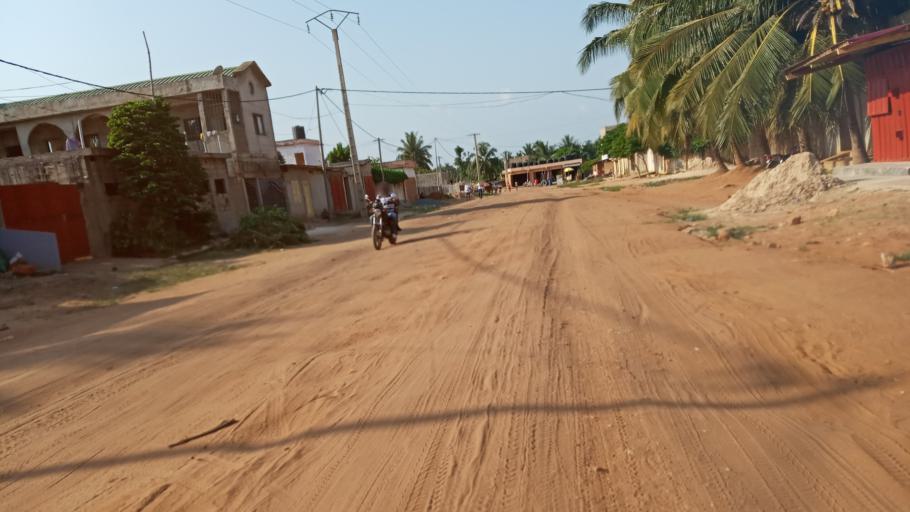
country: TG
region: Maritime
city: Lome
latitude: 6.1782
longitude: 1.1510
